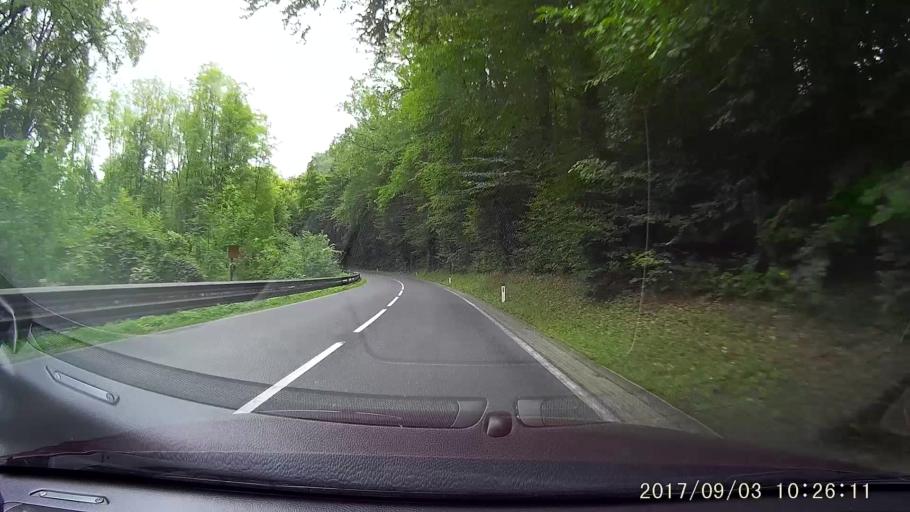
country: AT
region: Styria
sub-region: Politischer Bezirk Hartberg-Fuerstenfeld
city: Ilz
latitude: 47.0773
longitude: 15.9219
